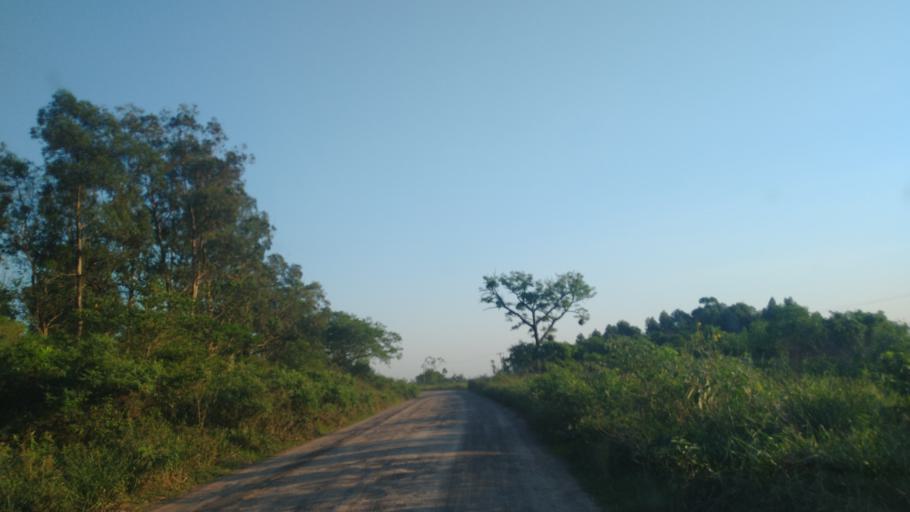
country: PY
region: Neembucu
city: Cerrito
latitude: -27.3971
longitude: -57.6584
